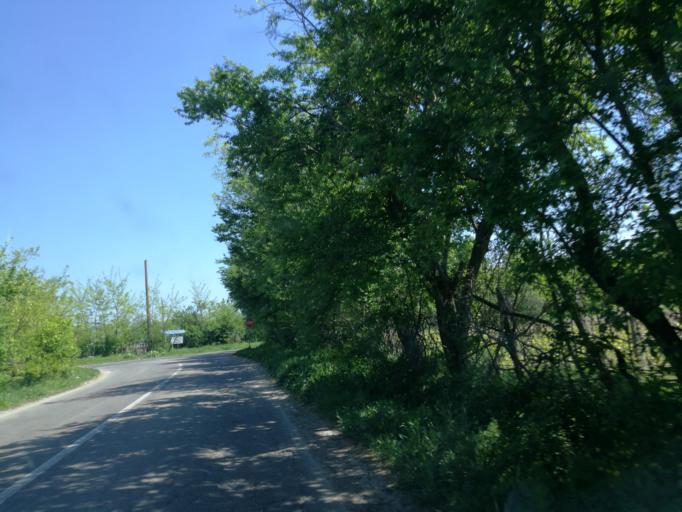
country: RO
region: Ialomita
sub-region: Comuna Adancata
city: Adancata
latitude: 44.7614
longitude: 26.4467
